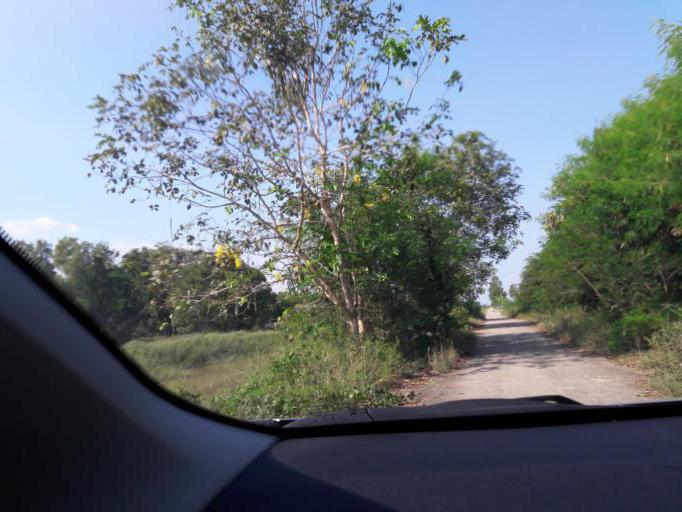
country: TH
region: Ang Thong
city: Ang Thong
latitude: 14.5462
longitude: 100.4068
